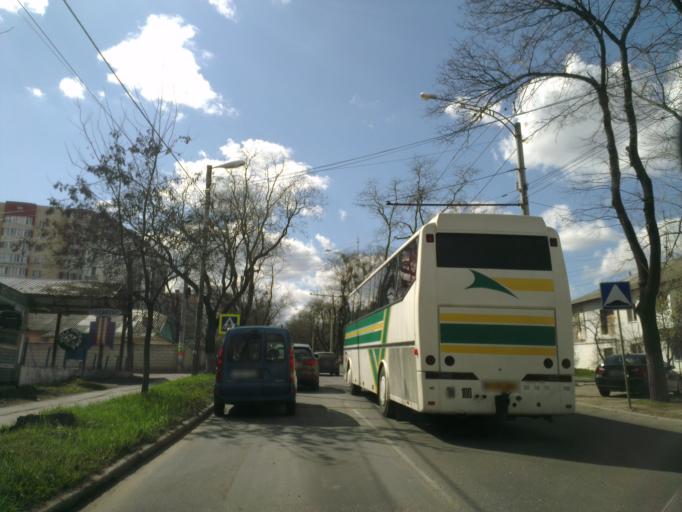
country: MD
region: Chisinau
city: Chisinau
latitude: 47.0043
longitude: 28.8200
